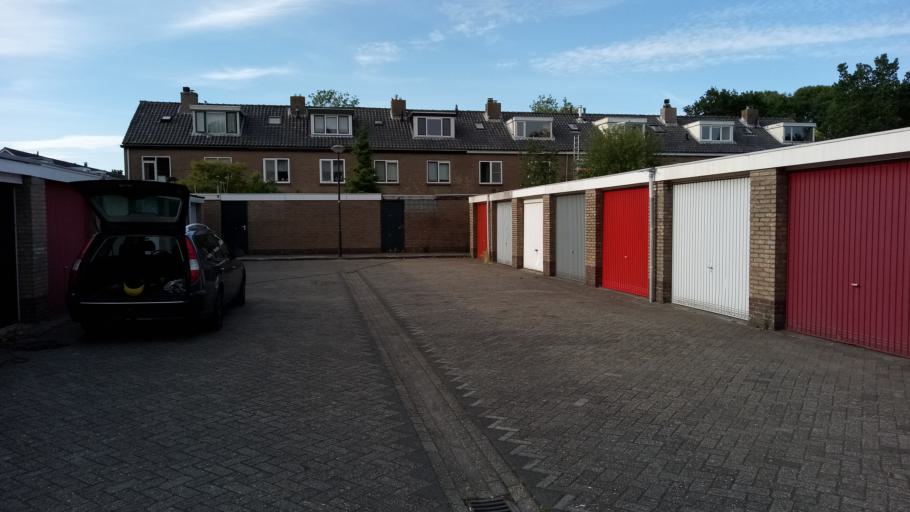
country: NL
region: North Holland
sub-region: Gemeente Heerhugowaard
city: Heerhugowaard
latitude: 52.6771
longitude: 4.8557
